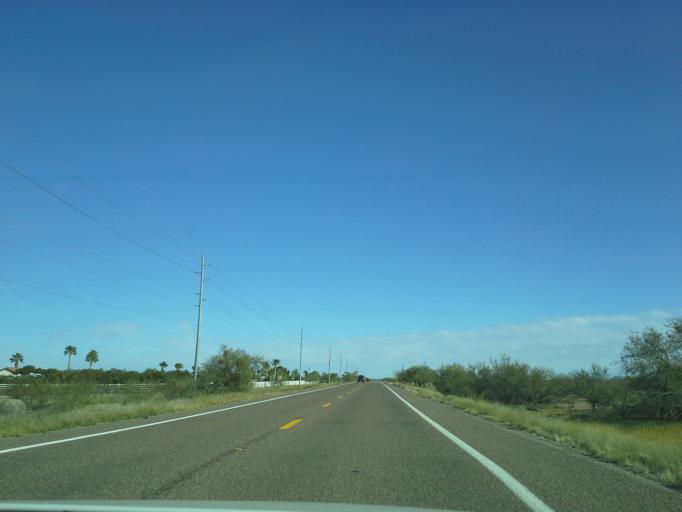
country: US
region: Arizona
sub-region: Yavapai County
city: Congress
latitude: 33.9429
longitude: -113.0148
